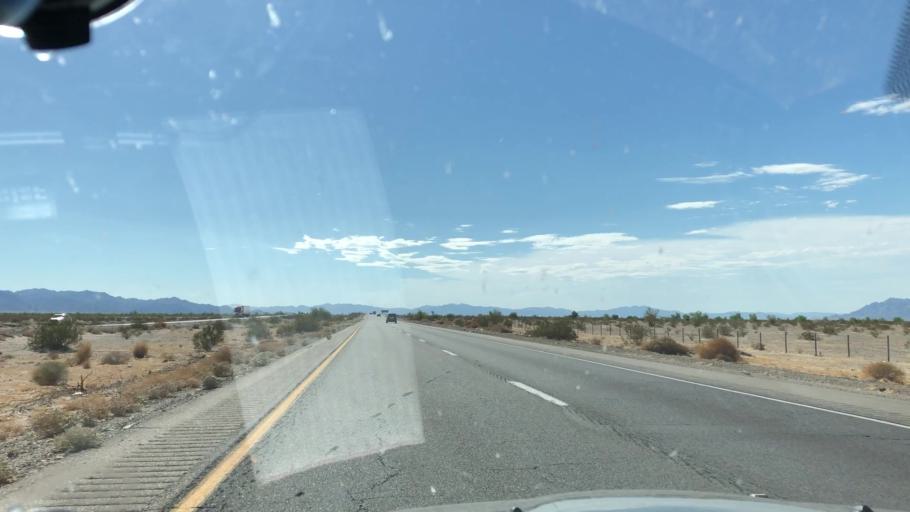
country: US
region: California
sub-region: Riverside County
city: Mesa Verde
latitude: 33.6498
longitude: -115.1325
